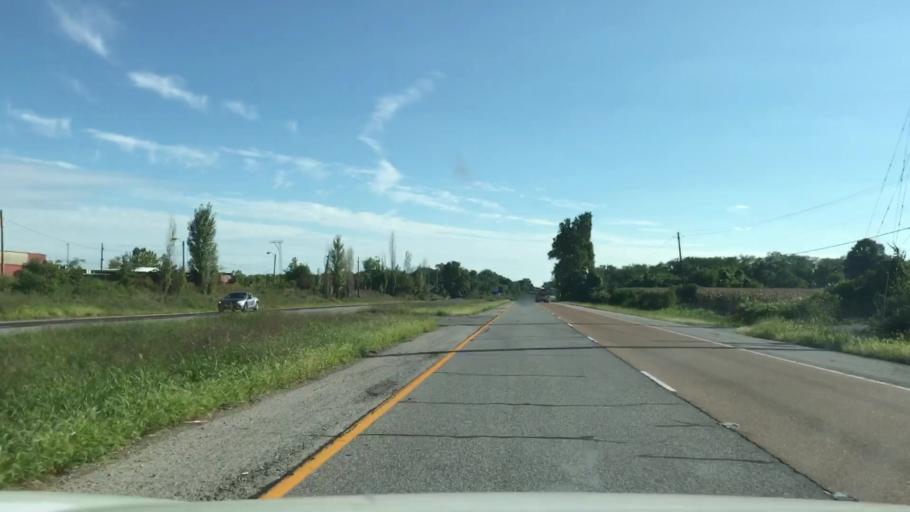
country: US
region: Illinois
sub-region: Madison County
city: Hartford
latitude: 38.7993
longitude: -90.1010
